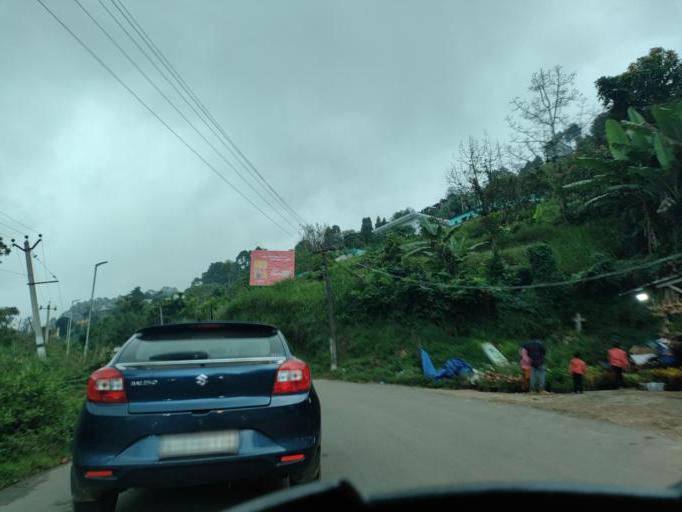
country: IN
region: Tamil Nadu
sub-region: Dindigul
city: Kodaikanal
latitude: 10.2374
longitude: 77.5070
